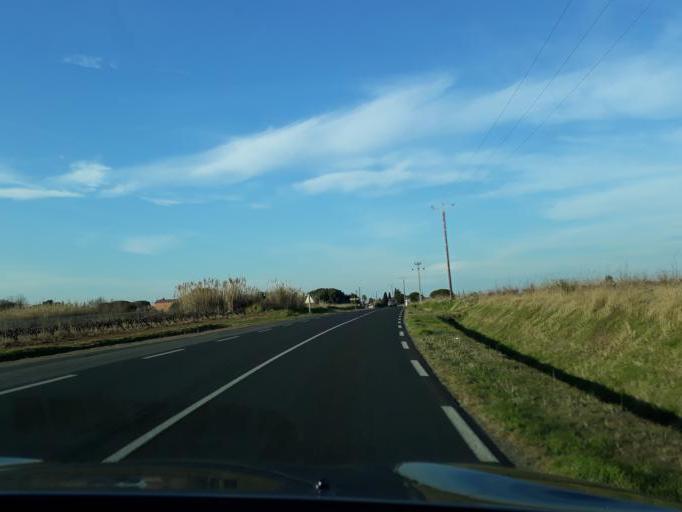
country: FR
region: Languedoc-Roussillon
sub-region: Departement de l'Herault
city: Marseillan
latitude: 43.3306
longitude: 3.5253
